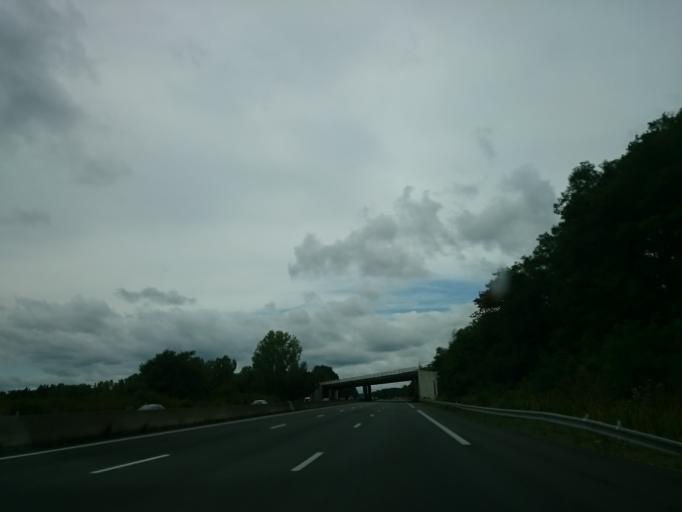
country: FR
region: Pays de la Loire
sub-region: Departement de la Sarthe
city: Le Luart
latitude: 48.1207
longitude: 0.6023
